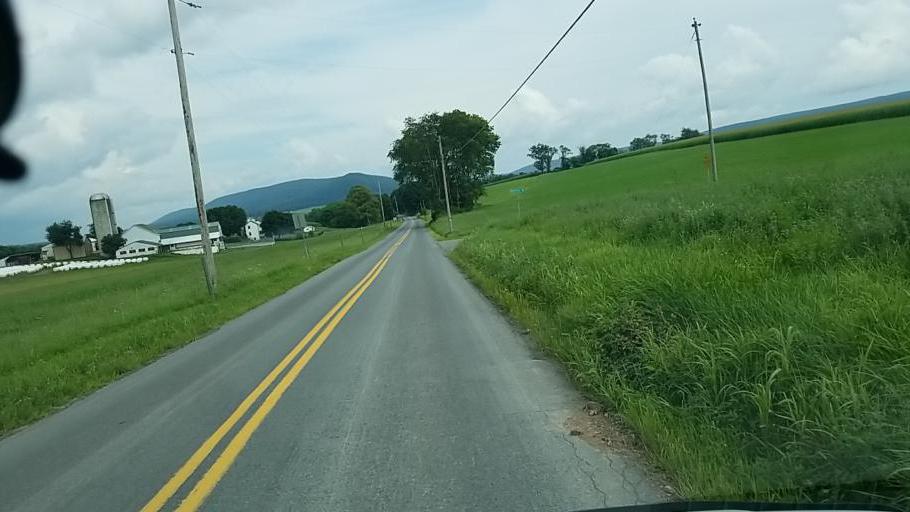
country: US
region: Pennsylvania
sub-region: Dauphin County
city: Elizabethville
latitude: 40.5802
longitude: -76.8113
